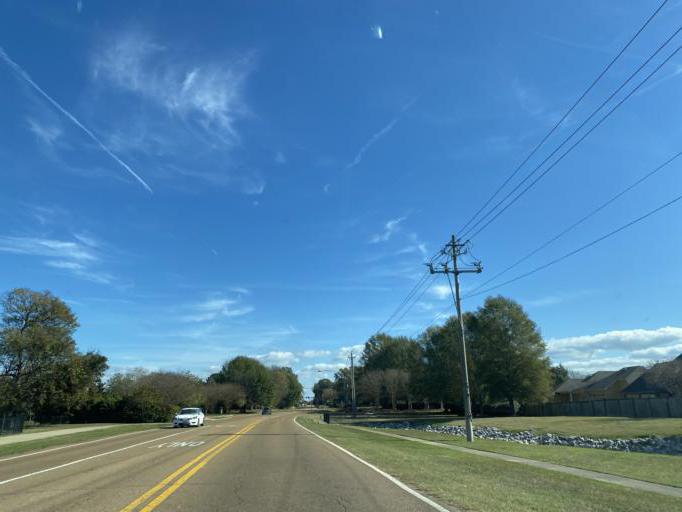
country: US
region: Mississippi
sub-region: Madison County
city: Madison
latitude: 32.4576
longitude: -90.1062
